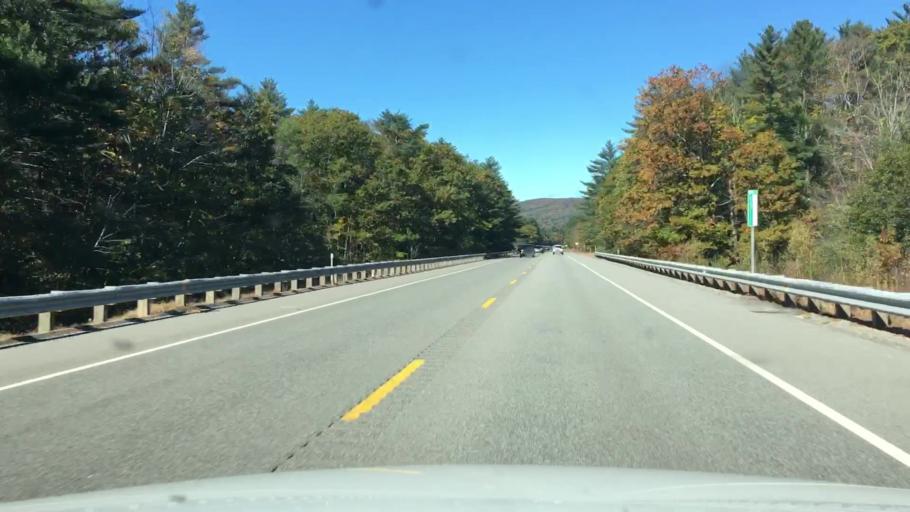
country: US
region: New Hampshire
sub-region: Carroll County
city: Sanbornville
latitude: 43.4907
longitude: -71.0155
